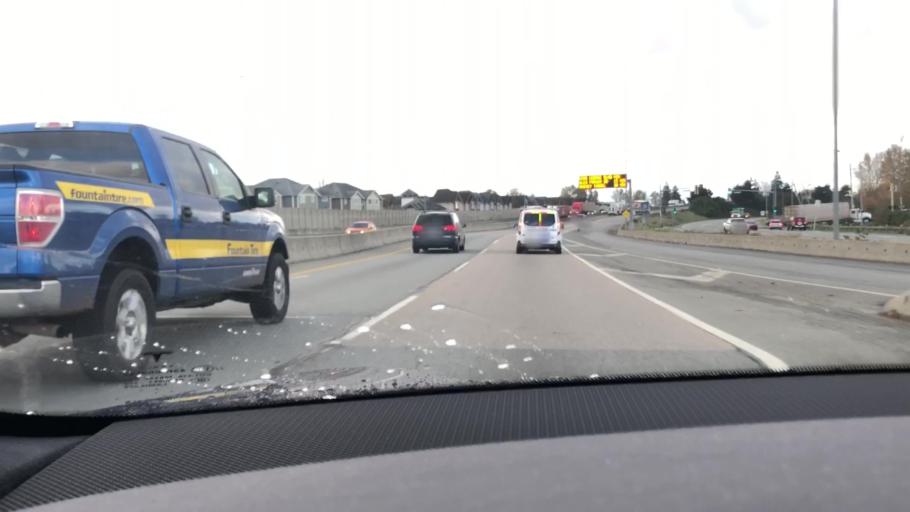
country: CA
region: British Columbia
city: New Westminster
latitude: 49.1860
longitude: -122.9504
